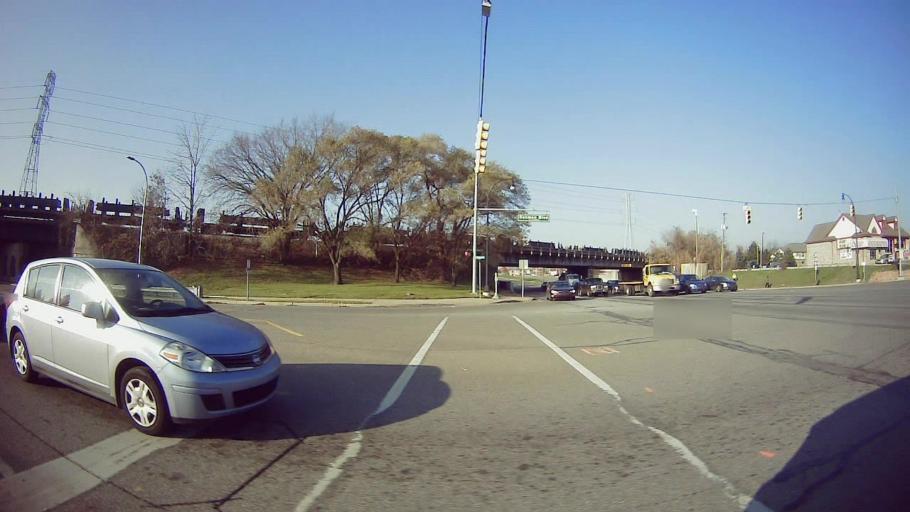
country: US
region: Michigan
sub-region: Wayne County
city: Dearborn
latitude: 42.3286
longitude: -83.1688
